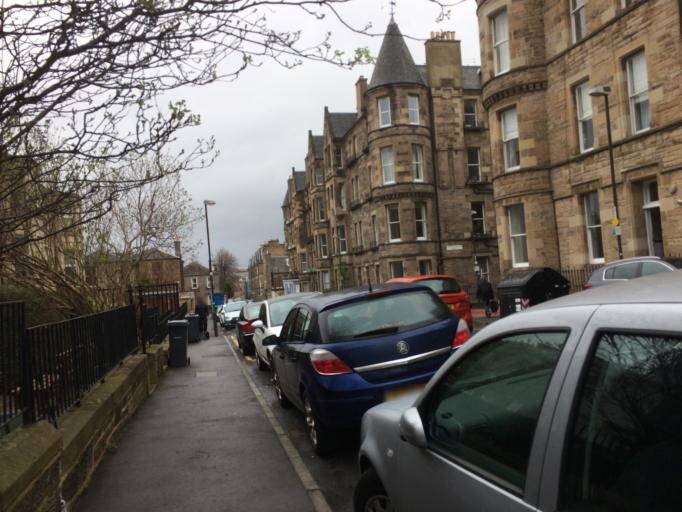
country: GB
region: Scotland
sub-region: Edinburgh
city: Edinburgh
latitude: 55.9399
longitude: -3.2091
